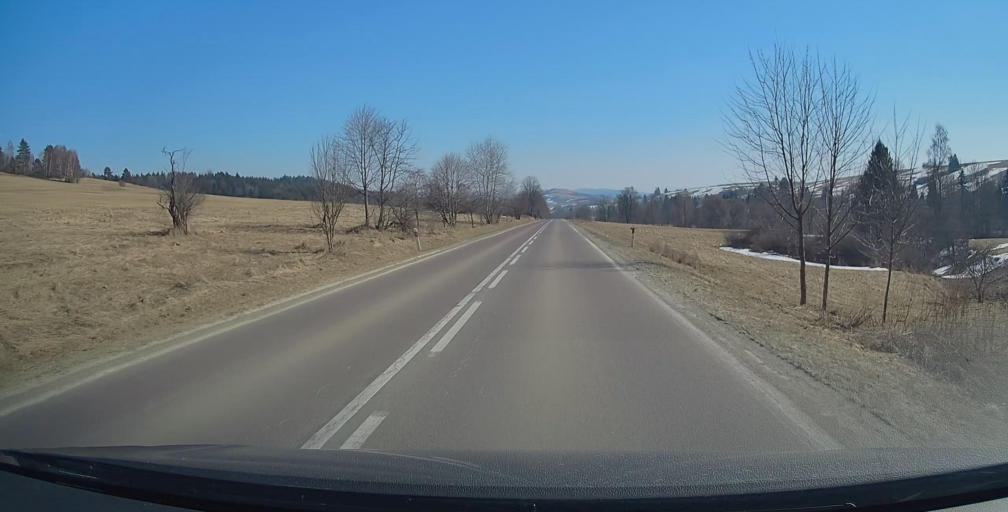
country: PL
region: Subcarpathian Voivodeship
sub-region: Powiat bieszczadzki
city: Ustrzyki Dolne
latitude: 49.5166
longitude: 22.6067
